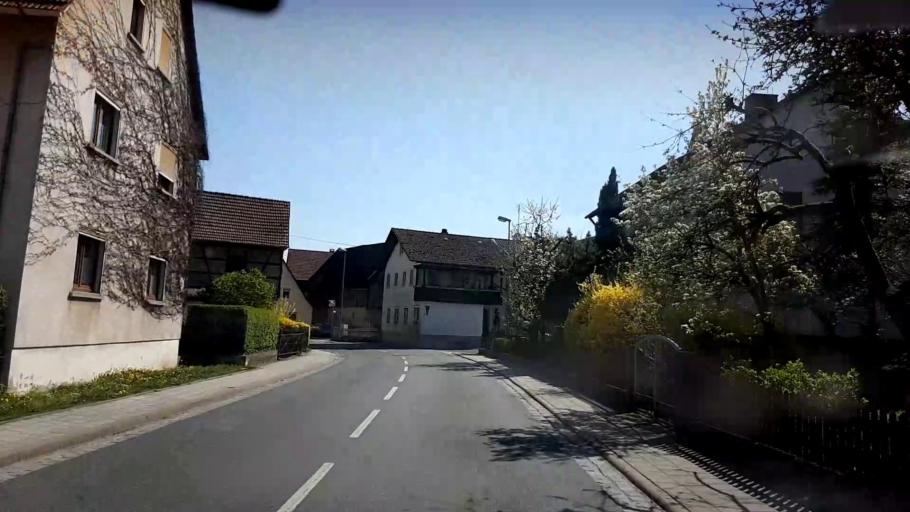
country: DE
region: Bavaria
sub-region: Upper Franconia
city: Unterleinleiter
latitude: 49.8233
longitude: 11.1902
